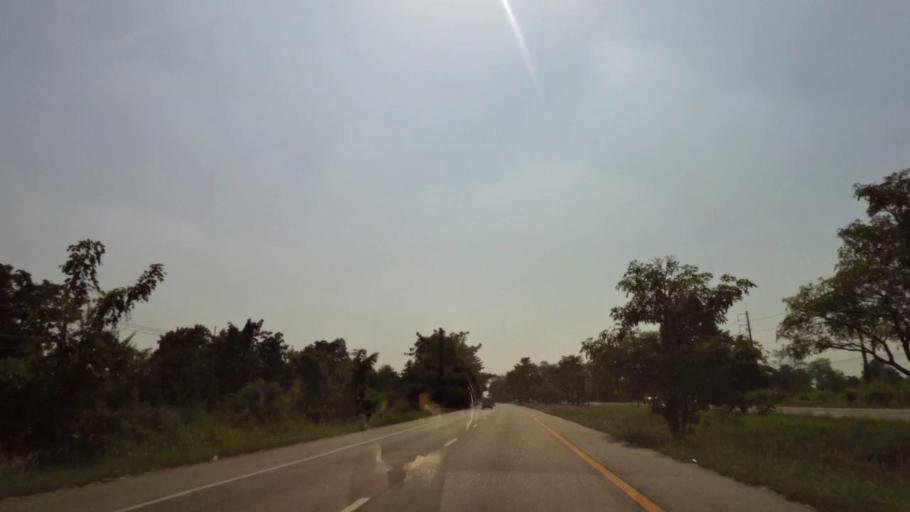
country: TH
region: Phichit
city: Wachira Barami
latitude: 16.6386
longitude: 100.1496
